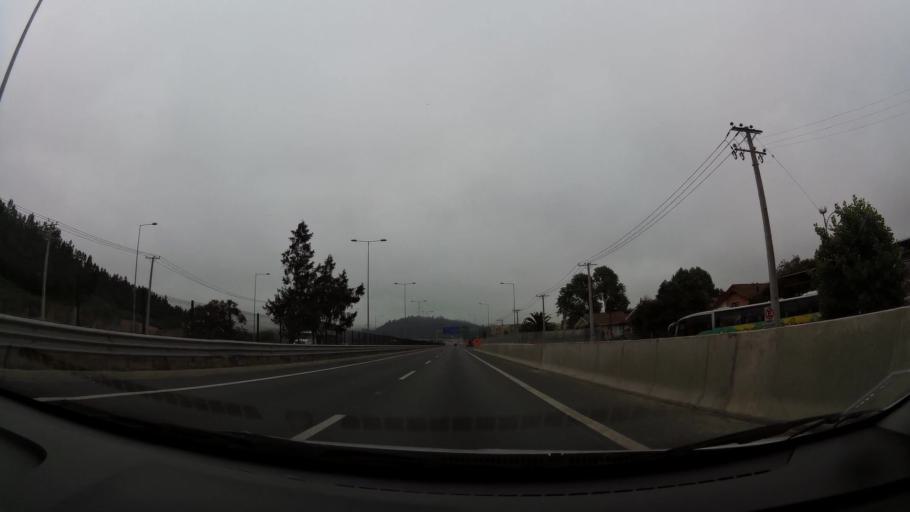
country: CL
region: Biobio
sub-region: Provincia de Concepcion
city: Concepcion
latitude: -36.8146
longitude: -73.0214
